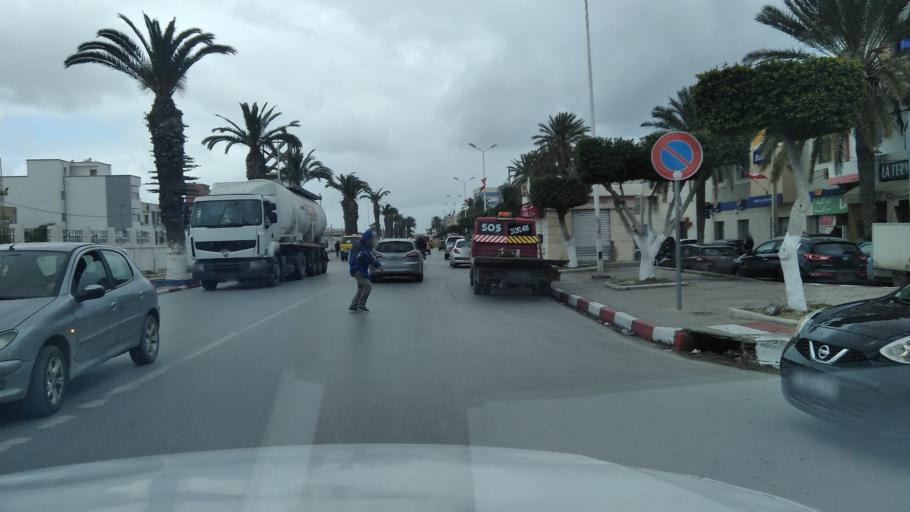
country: TN
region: Bin 'Arus
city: Ben Arous
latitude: 36.7538
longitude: 10.2225
